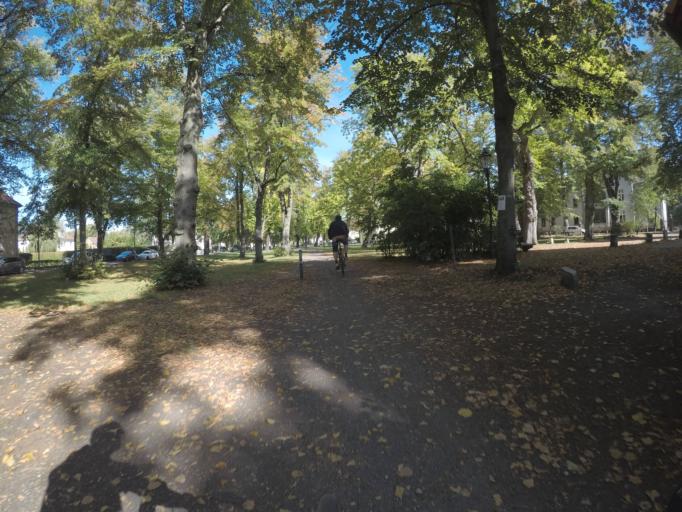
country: DE
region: Berlin
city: Konradshohe
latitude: 52.6085
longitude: 13.2132
